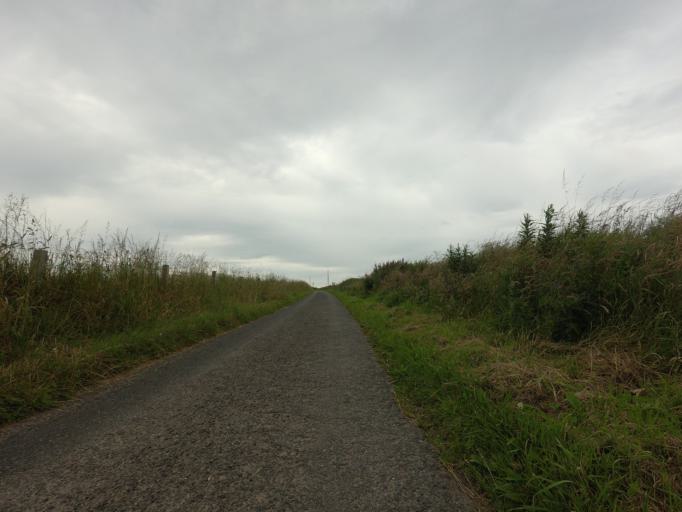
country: GB
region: Scotland
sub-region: Aberdeenshire
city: Whitehills
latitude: 57.6755
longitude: -2.5971
